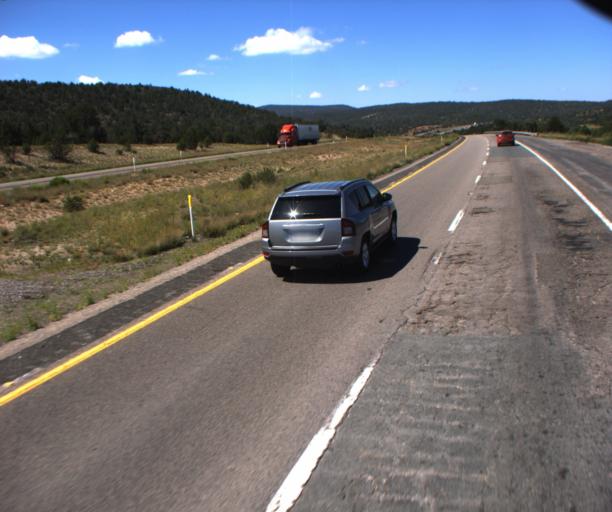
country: US
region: Arizona
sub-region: Mohave County
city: Peach Springs
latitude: 35.2999
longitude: -113.0221
